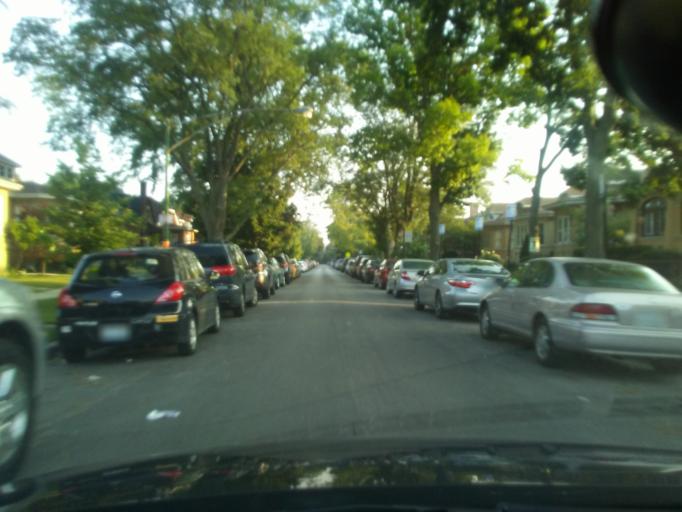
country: US
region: Illinois
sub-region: Cook County
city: Lincolnwood
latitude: 42.0016
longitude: -87.6985
